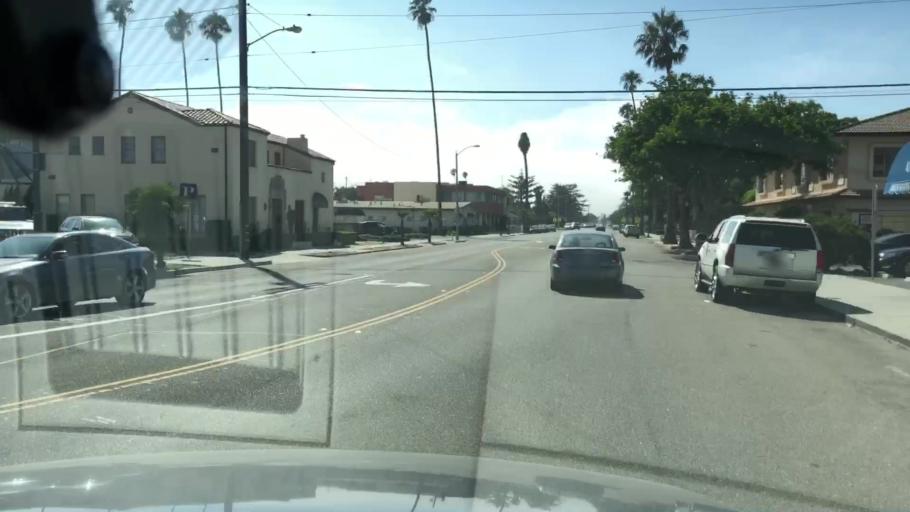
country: US
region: California
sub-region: Ventura County
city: Oxnard
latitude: 34.1977
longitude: -119.1813
